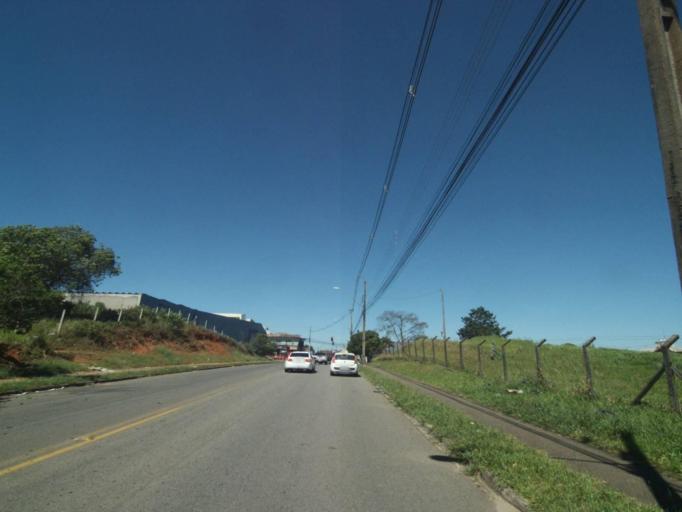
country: BR
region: Parana
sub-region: Curitiba
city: Curitiba
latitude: -25.4639
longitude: -49.3466
